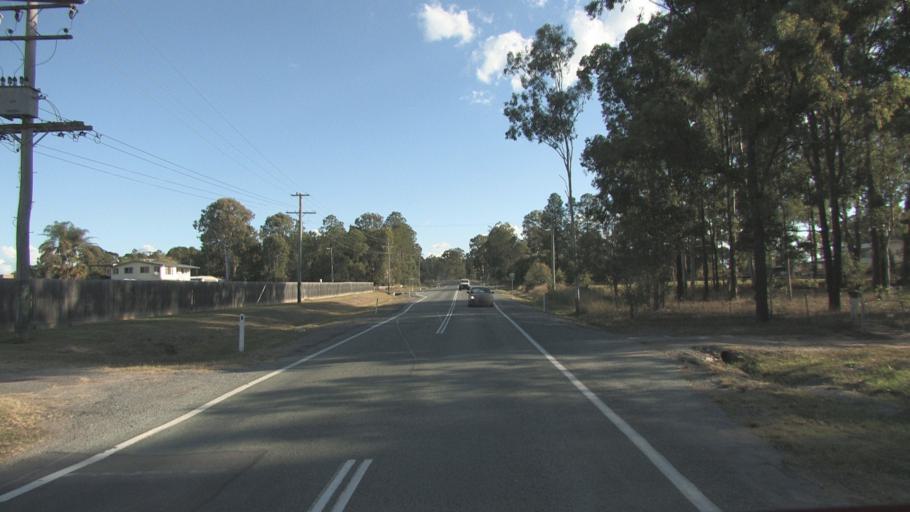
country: AU
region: Queensland
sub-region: Logan
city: Park Ridge South
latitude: -27.7175
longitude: 152.9713
